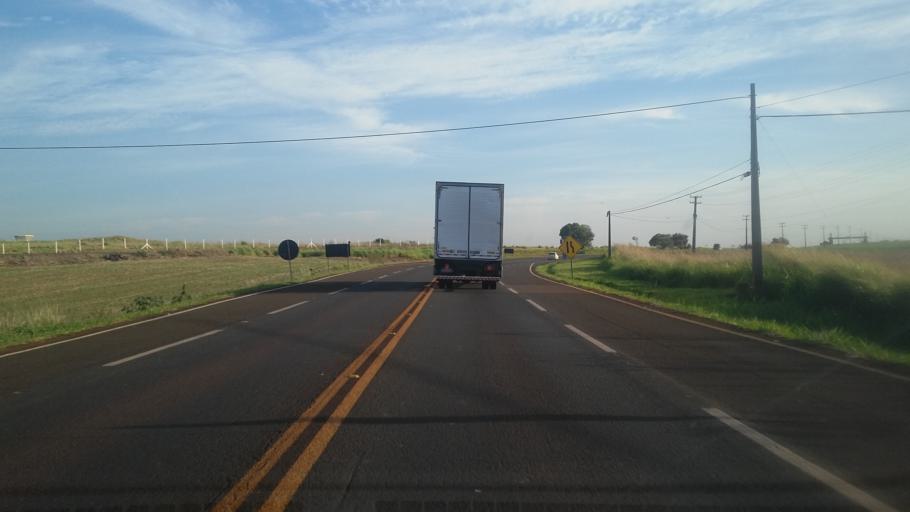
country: BR
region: Parana
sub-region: Bandeirantes
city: Bandeirantes
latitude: -23.1589
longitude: -50.6076
